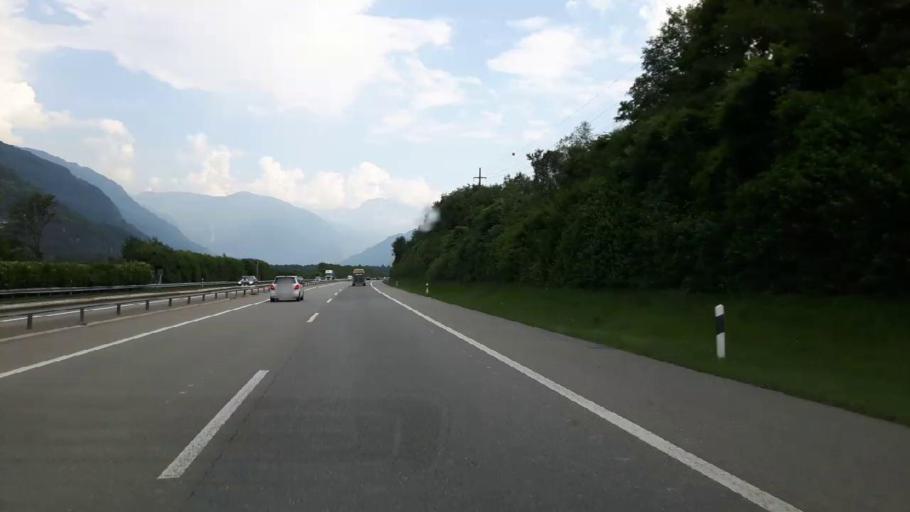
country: CH
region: Ticino
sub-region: Riviera District
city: Lodrino
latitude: 46.3004
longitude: 8.9872
